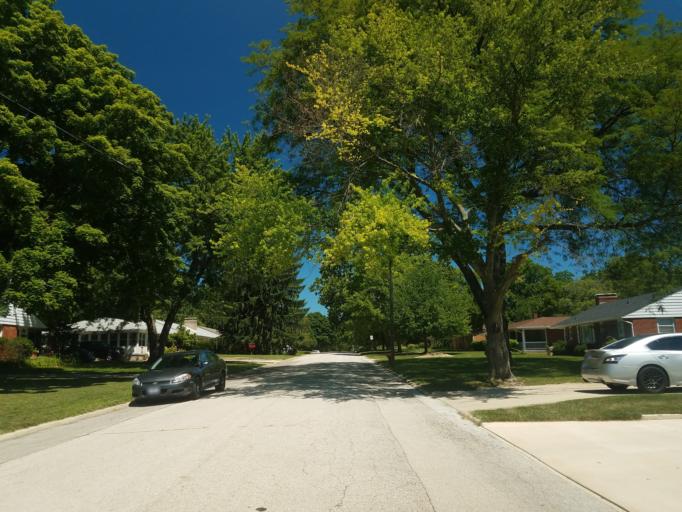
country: US
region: Illinois
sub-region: McLean County
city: Normal
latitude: 40.5104
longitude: -89.0032
